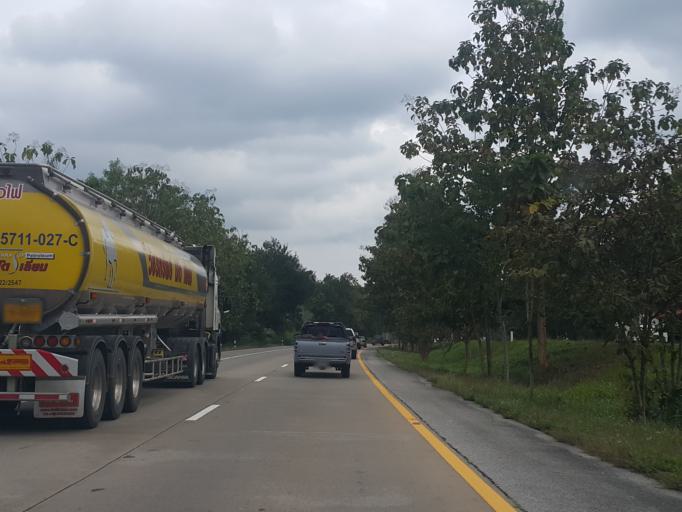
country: TH
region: Lamphun
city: Mae Tha
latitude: 18.4761
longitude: 99.1272
